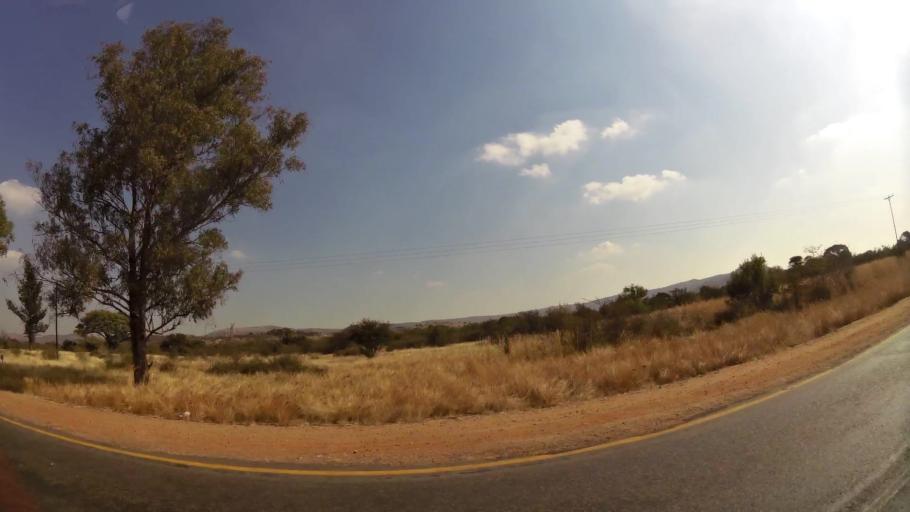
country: ZA
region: North-West
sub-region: Bojanala Platinum District Municipality
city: Rustenburg
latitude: -25.5149
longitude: 27.1007
